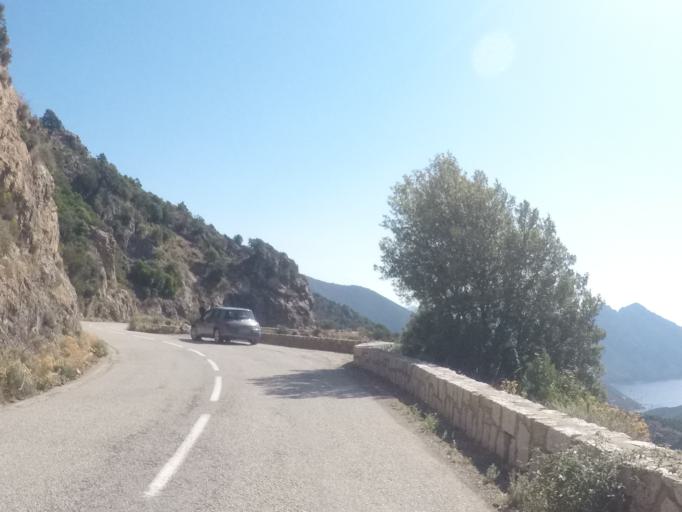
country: FR
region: Corsica
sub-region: Departement de la Haute-Corse
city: Calvi
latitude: 42.3630
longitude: 8.6483
